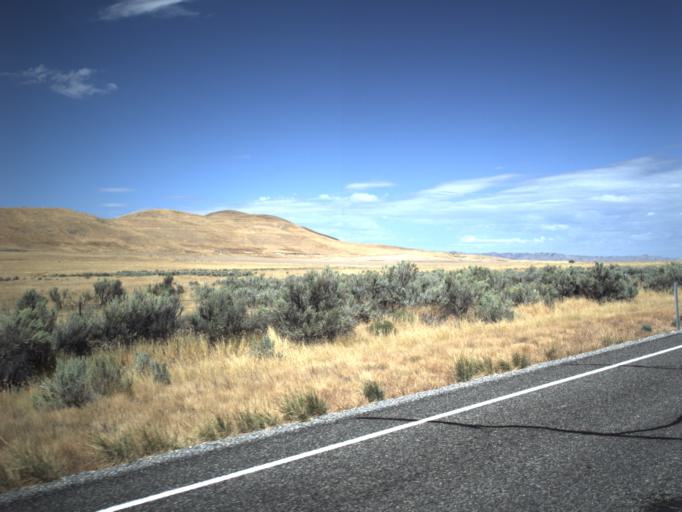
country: US
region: Utah
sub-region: Box Elder County
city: Garland
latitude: 41.8002
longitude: -112.4163
